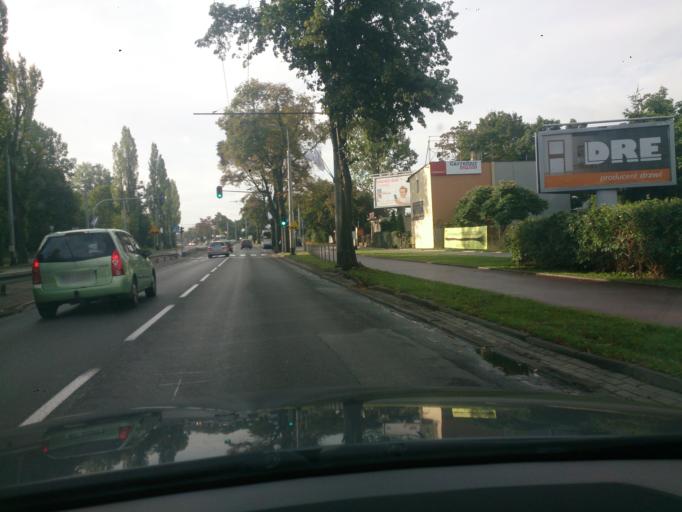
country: PL
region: Pomeranian Voivodeship
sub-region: Gdynia
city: Gdynia
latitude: 54.5029
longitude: 18.5363
